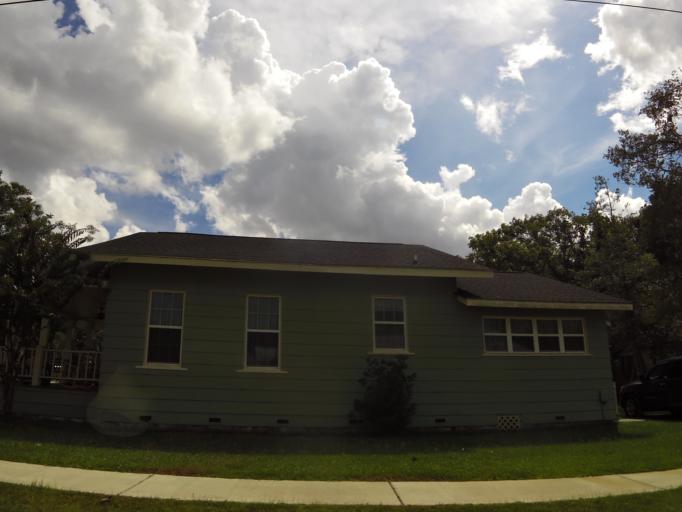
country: US
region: Georgia
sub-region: Brantley County
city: Nahunta
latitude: 31.2064
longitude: -81.9828
